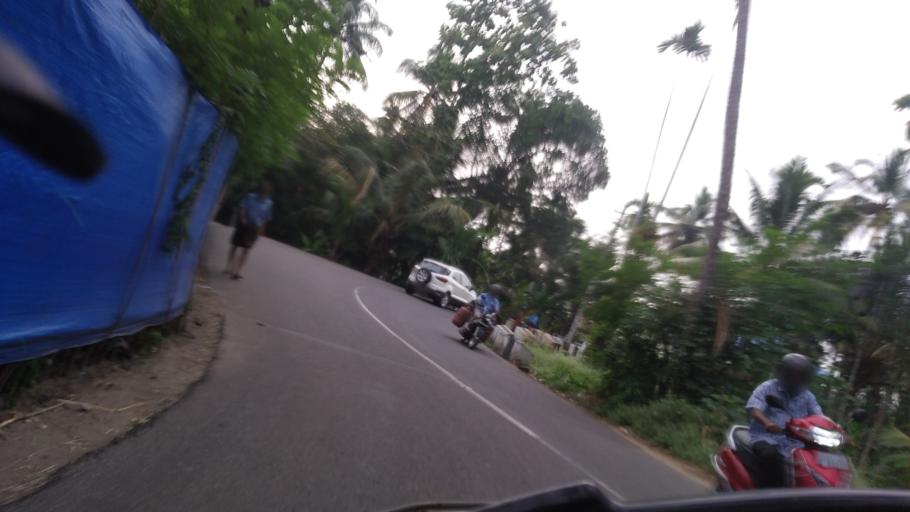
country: IN
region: Kerala
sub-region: Thrissur District
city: Kodungallur
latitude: 10.1399
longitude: 76.2185
